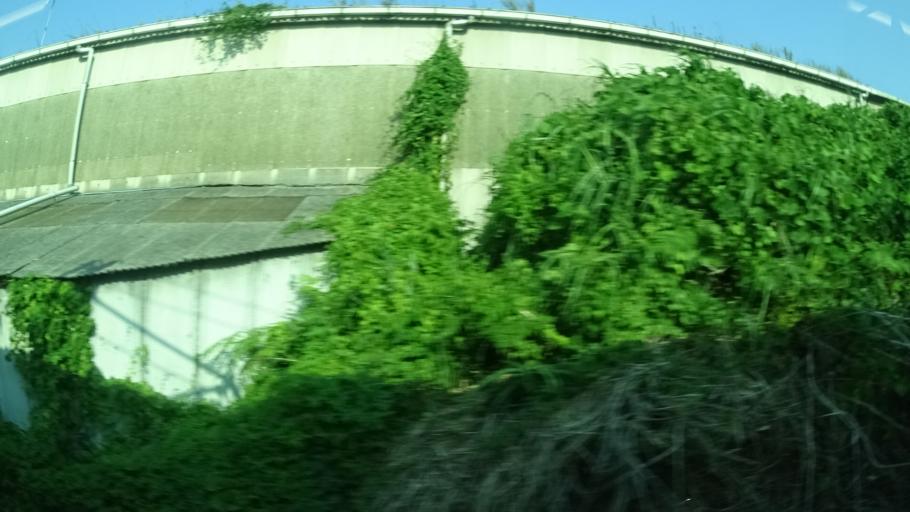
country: JP
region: Ibaraki
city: Kitaibaraki
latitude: 36.8127
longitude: 140.7638
